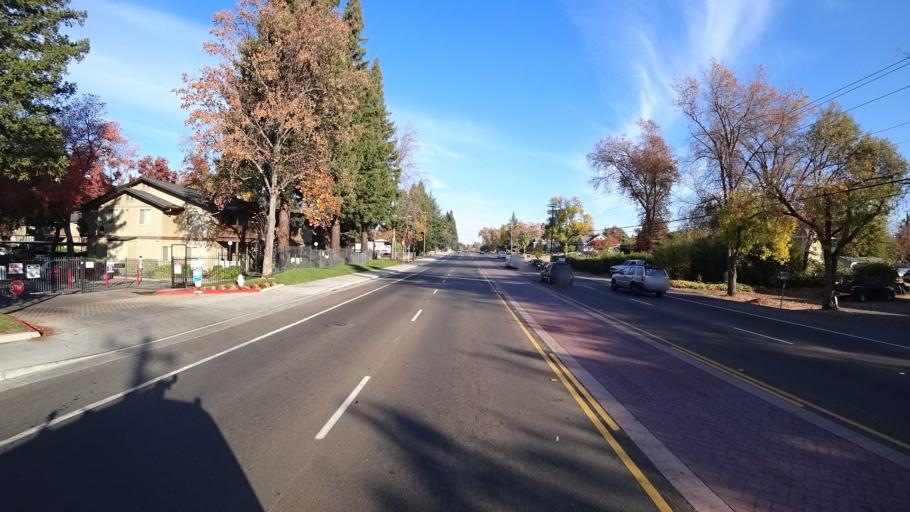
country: US
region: California
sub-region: Sacramento County
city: Citrus Heights
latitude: 38.7107
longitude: -121.2719
